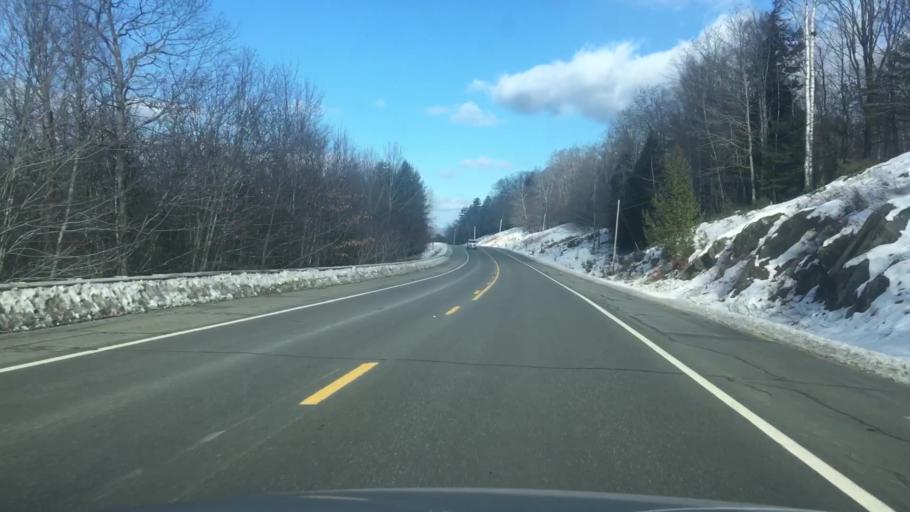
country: US
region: Maine
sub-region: Somerset County
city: Madison
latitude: 45.0030
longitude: -69.8582
